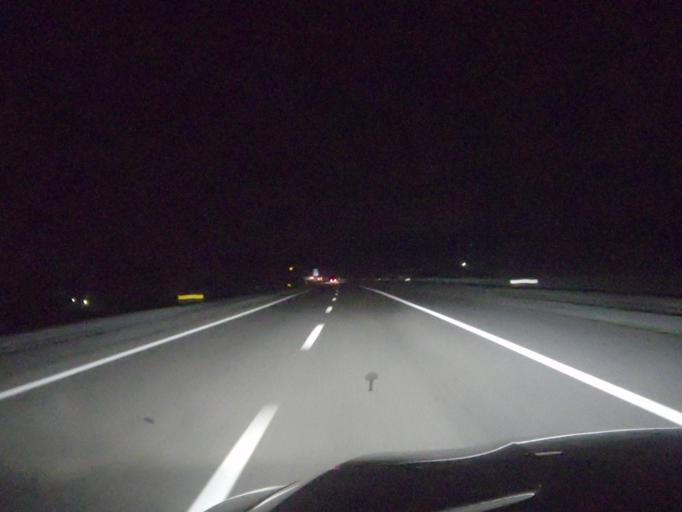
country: PT
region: Coimbra
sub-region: Soure
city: Soure
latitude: 40.0231
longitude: -8.5913
